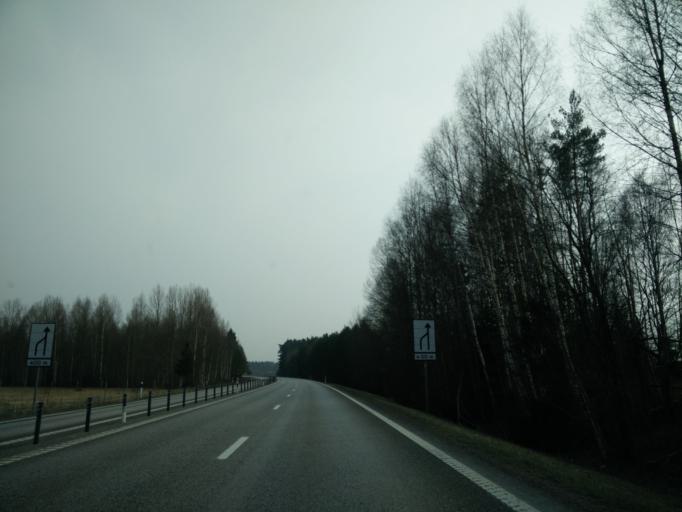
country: SE
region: Vaermland
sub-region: Forshaga Kommun
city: Forshaga
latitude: 59.4760
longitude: 13.4105
